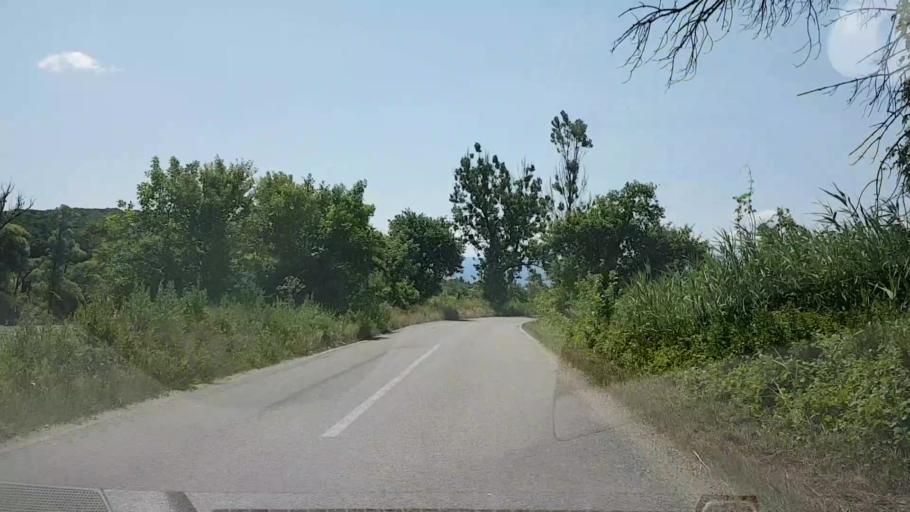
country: RO
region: Brasov
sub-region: Comuna Voila
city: Voila
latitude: 45.8530
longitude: 24.8314
